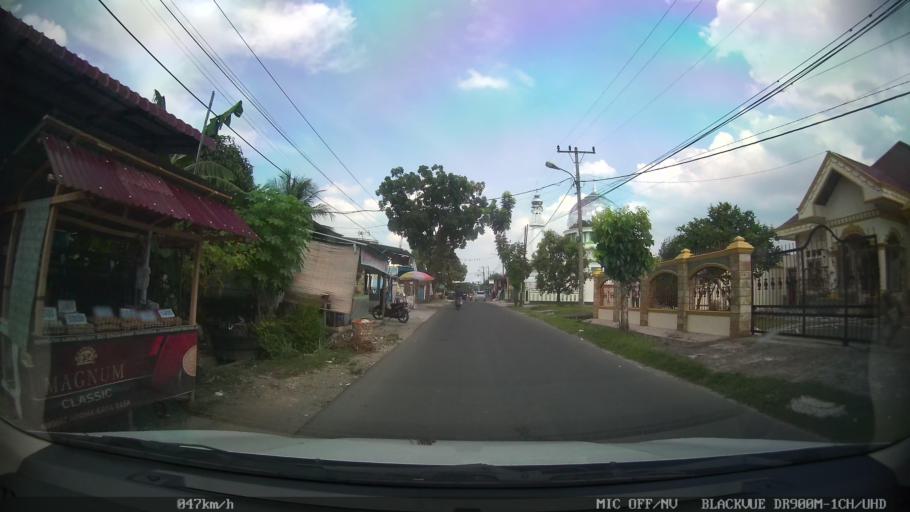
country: ID
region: North Sumatra
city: Binjai
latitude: 3.6131
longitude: 98.5078
